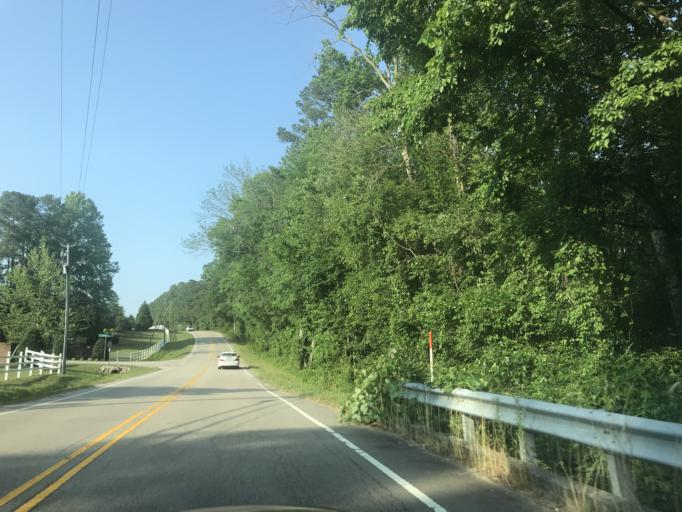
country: US
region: North Carolina
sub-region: Wake County
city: Knightdale
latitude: 35.8545
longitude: -78.4979
